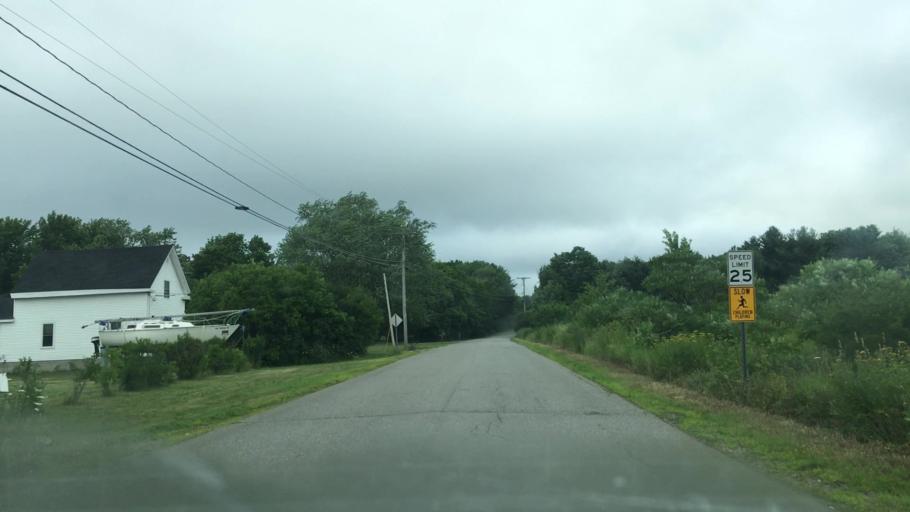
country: US
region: Maine
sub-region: Penobscot County
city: Veazie
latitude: 44.8434
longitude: -68.7459
